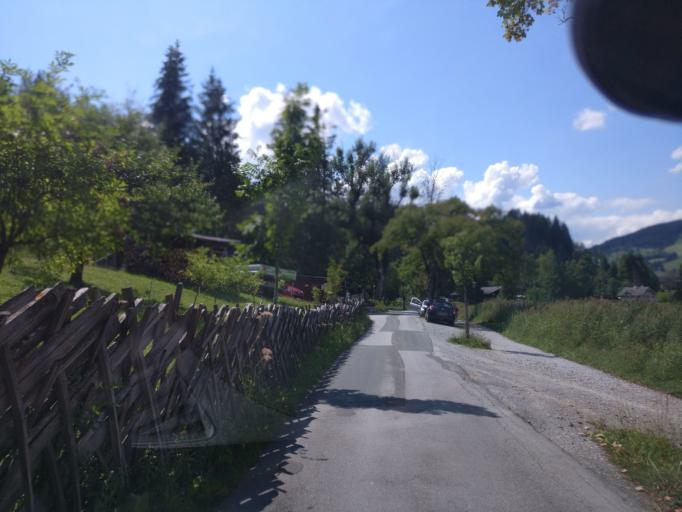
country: AT
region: Salzburg
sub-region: Politischer Bezirk Sankt Johann im Pongau
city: Goldegg
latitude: 47.3174
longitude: 13.1060
